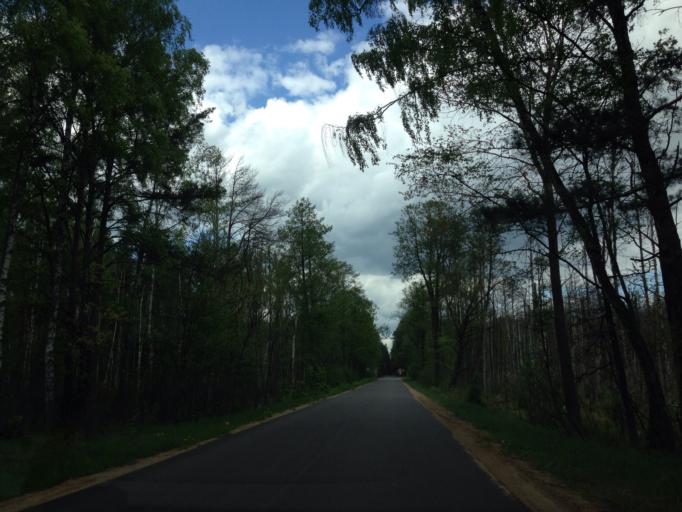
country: PL
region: Podlasie
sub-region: Powiat moniecki
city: Goniadz
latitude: 53.3497
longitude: 22.5976
